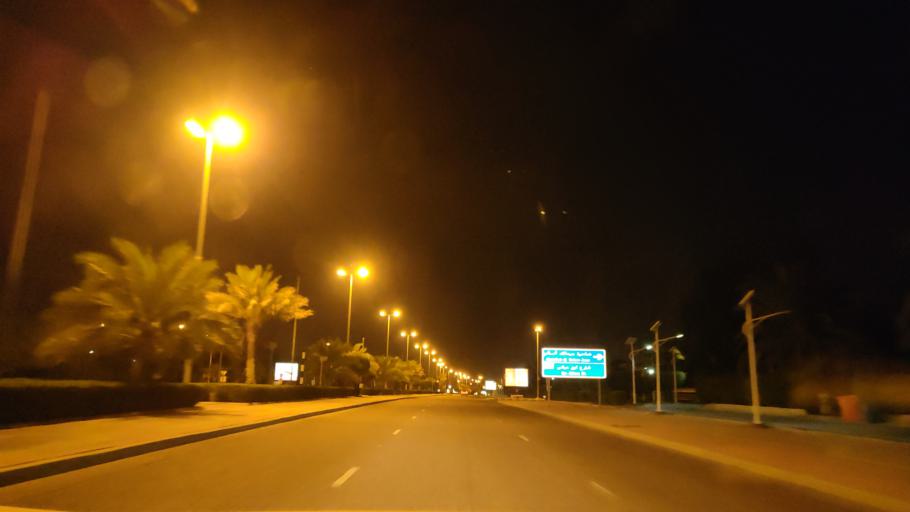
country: KW
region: Al Asimah
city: Ad Dasmah
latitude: 29.3481
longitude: 47.9894
